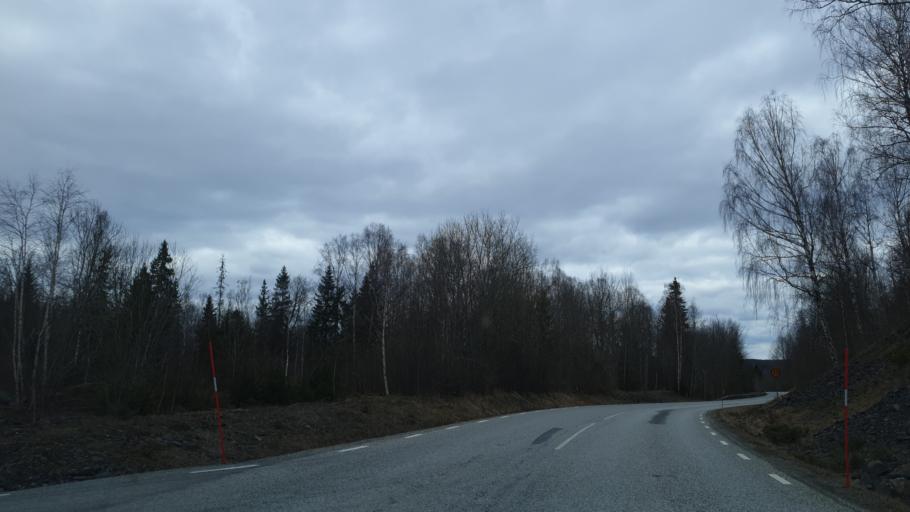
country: SE
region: OErebro
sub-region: Nora Kommun
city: As
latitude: 59.5988
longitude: 14.9188
